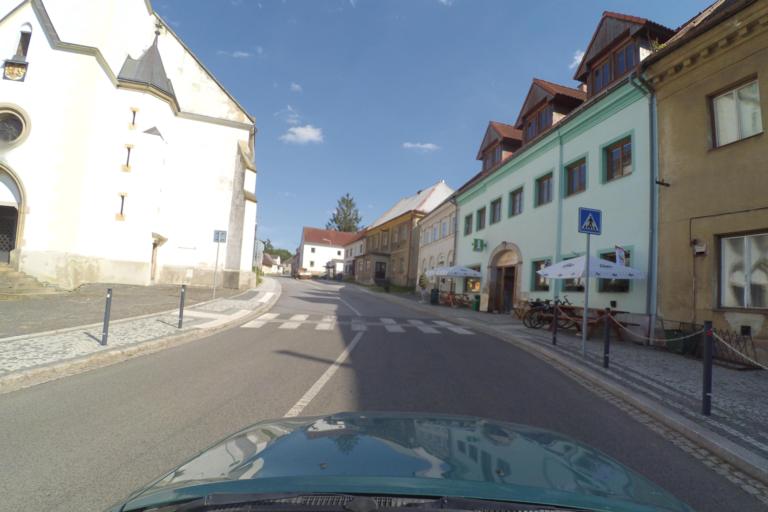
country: CZ
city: Osecna
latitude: 50.6945
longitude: 14.9209
